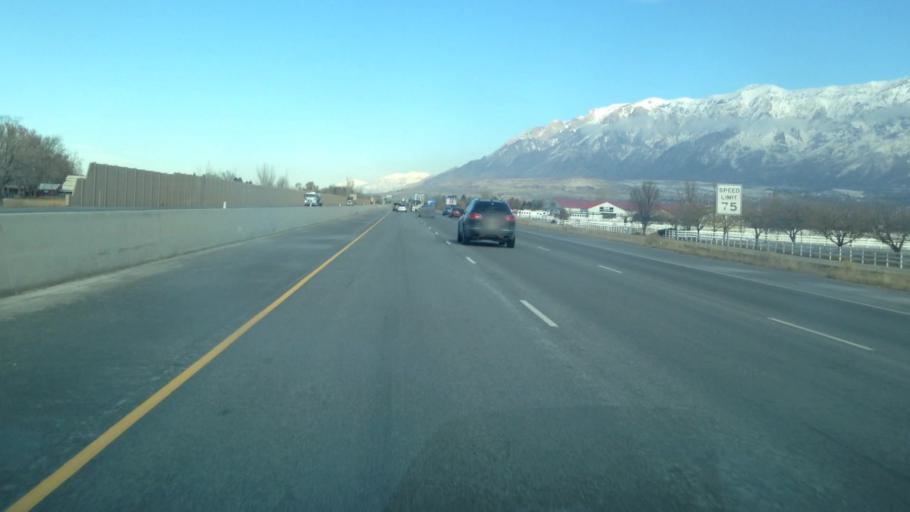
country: US
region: Utah
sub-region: Weber County
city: Farr West
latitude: 41.2786
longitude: -112.0261
